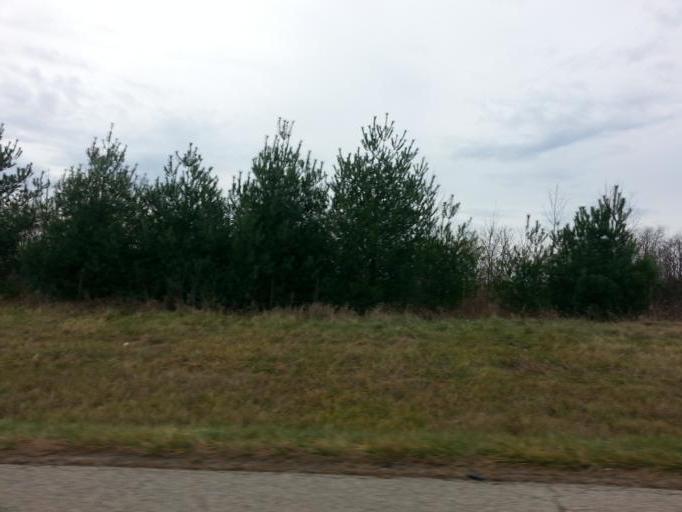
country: US
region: Indiana
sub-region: Decatur County
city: Greensburg
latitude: 39.3430
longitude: -85.4284
